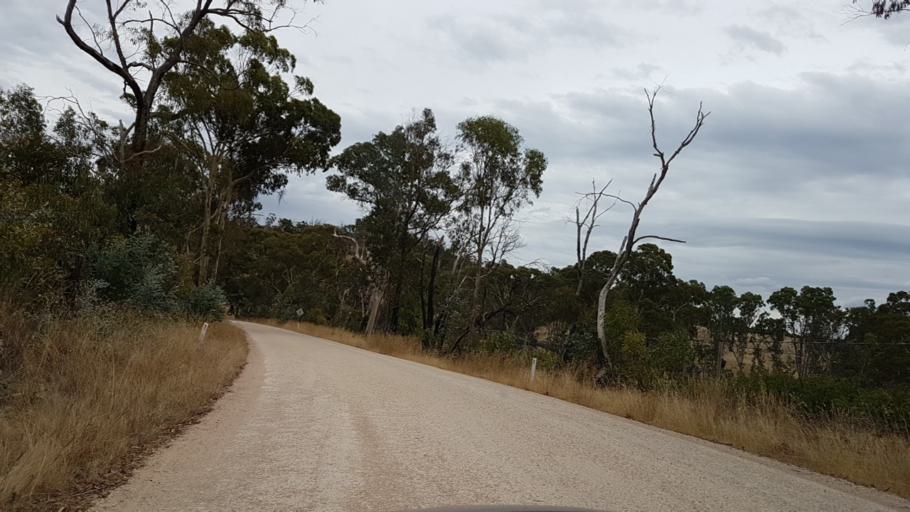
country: AU
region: South Australia
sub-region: Adelaide Hills
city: Gumeracha
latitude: -34.8028
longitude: 138.8338
